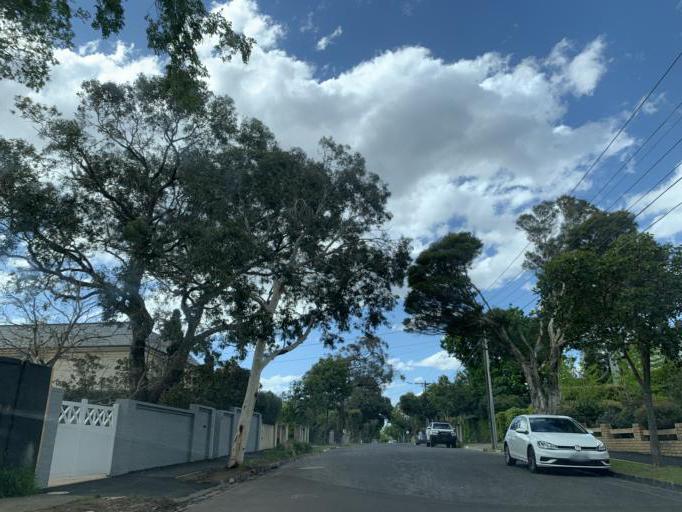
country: AU
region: Victoria
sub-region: Bayside
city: Hampton
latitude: -37.9232
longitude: 145.0040
